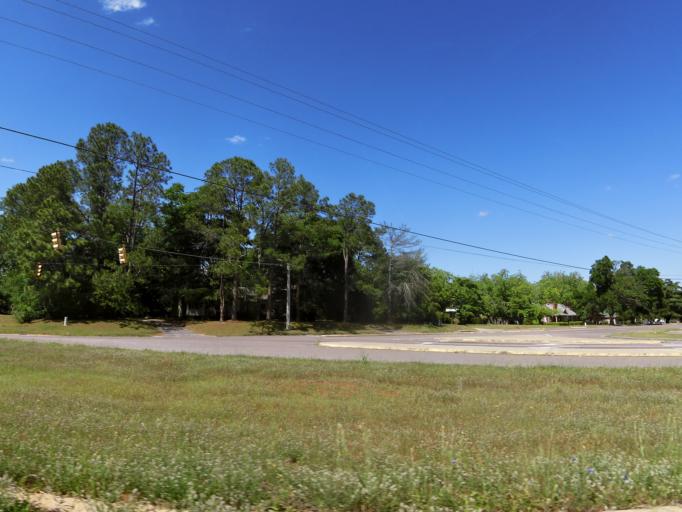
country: US
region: South Carolina
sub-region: Aiken County
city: Aiken
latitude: 33.5460
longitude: -81.6812
